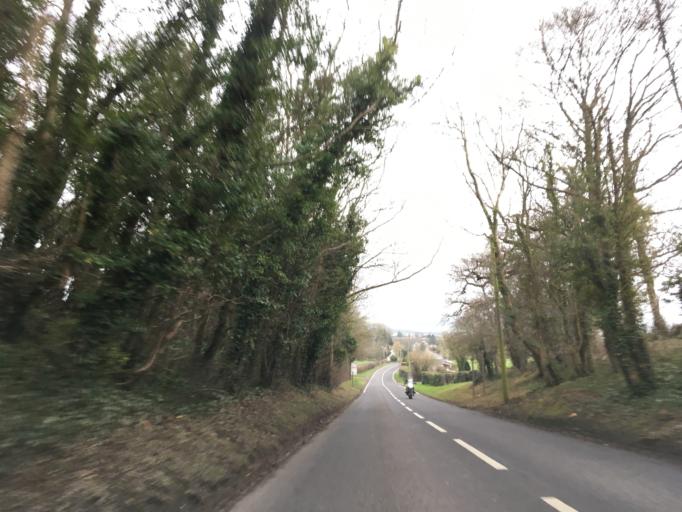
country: GB
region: England
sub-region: South Gloucestershire
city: Hinton
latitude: 51.5115
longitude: -2.4020
